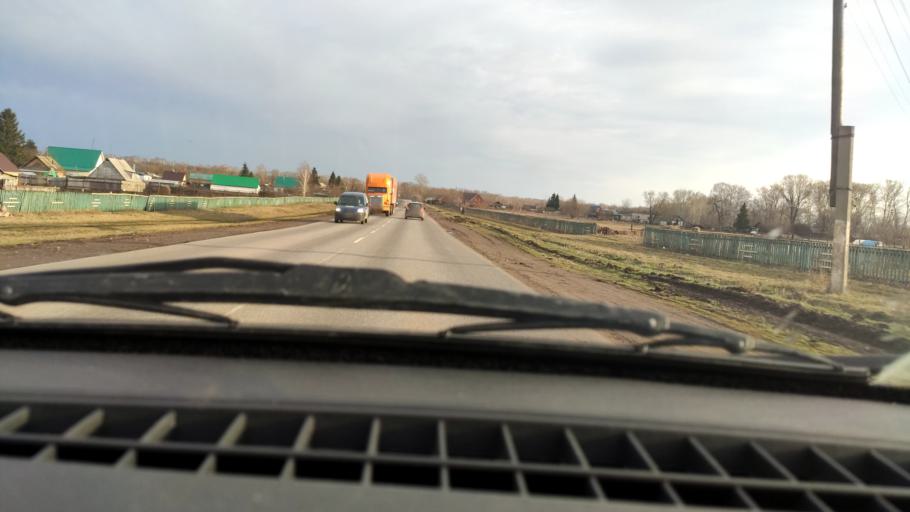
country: RU
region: Bashkortostan
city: Davlekanovo
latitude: 54.3709
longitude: 55.1953
